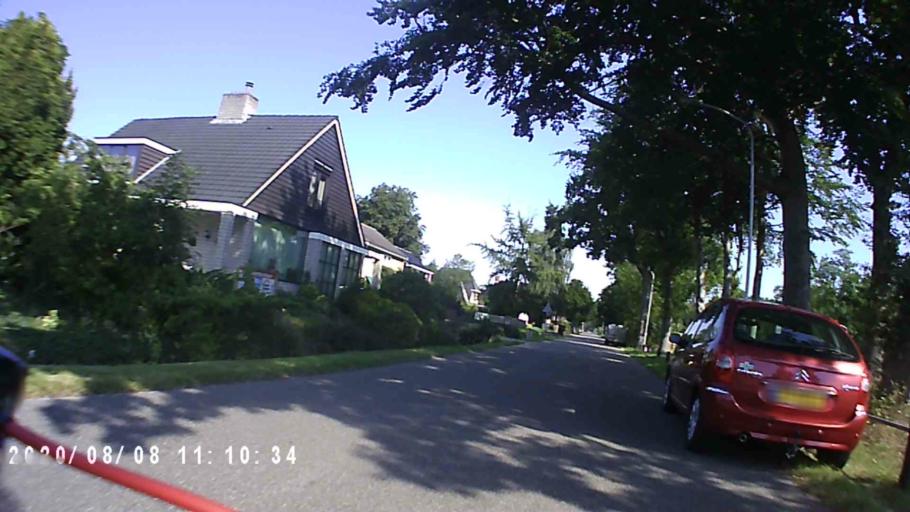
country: NL
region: Groningen
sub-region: Gemeente Leek
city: Leek
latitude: 53.1680
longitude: 6.3810
